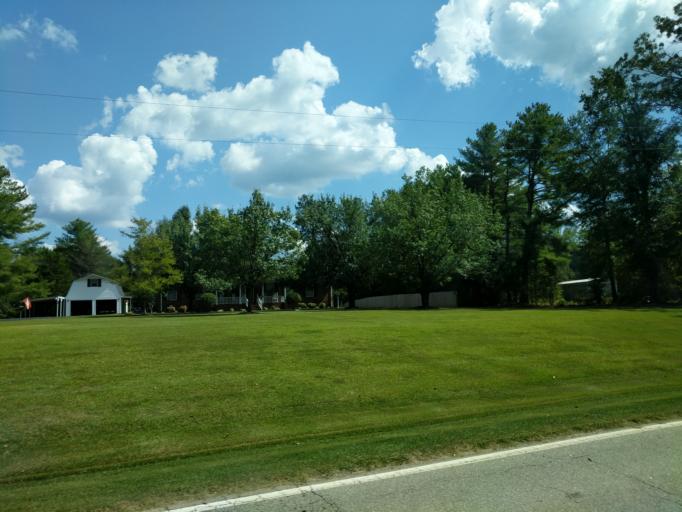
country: US
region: South Carolina
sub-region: Spartanburg County
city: Woodruff
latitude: 34.7127
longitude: -82.0468
